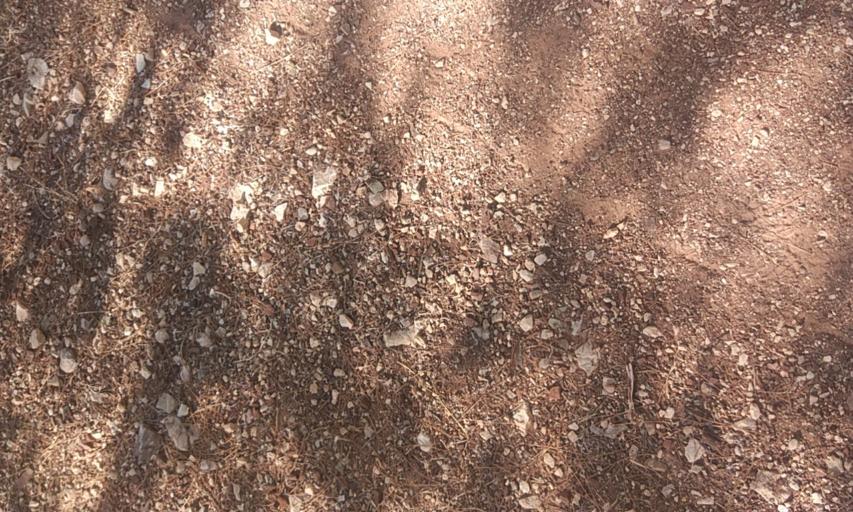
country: TR
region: Antalya
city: Altinyaka
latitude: 36.4884
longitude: 30.4241
